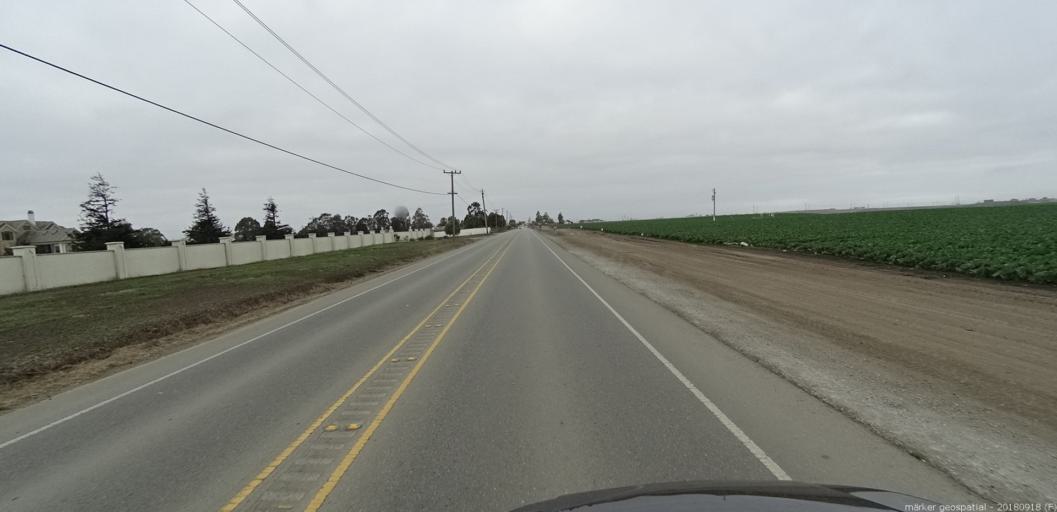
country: US
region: California
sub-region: Monterey County
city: Prunedale
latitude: 36.7480
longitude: -121.7082
